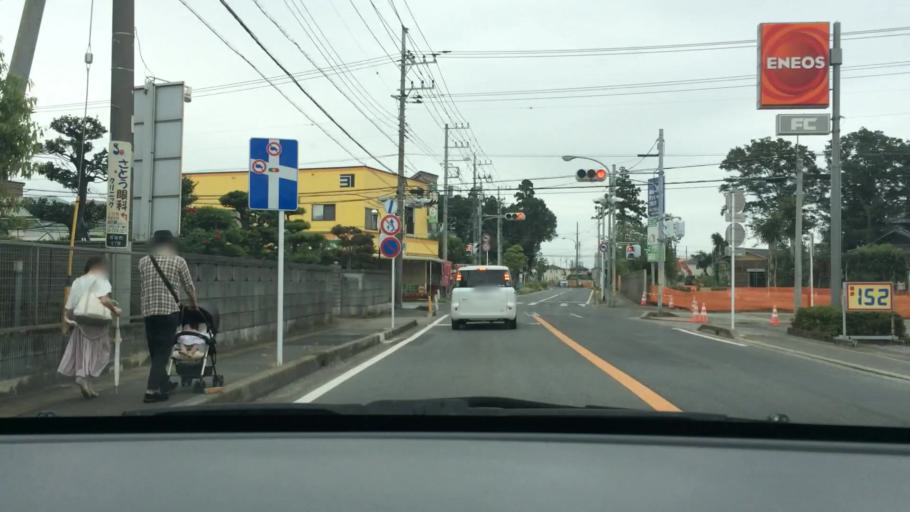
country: JP
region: Chiba
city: Nagareyama
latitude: 35.8776
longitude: 139.9191
